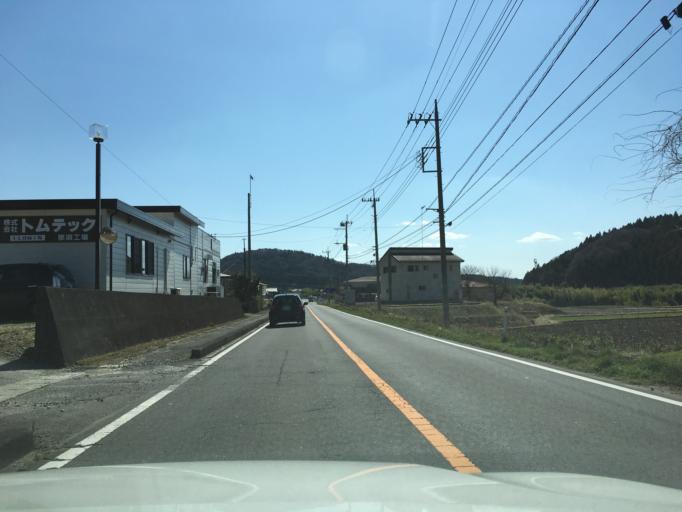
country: JP
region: Tochigi
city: Kuroiso
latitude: 36.9620
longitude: 140.1556
